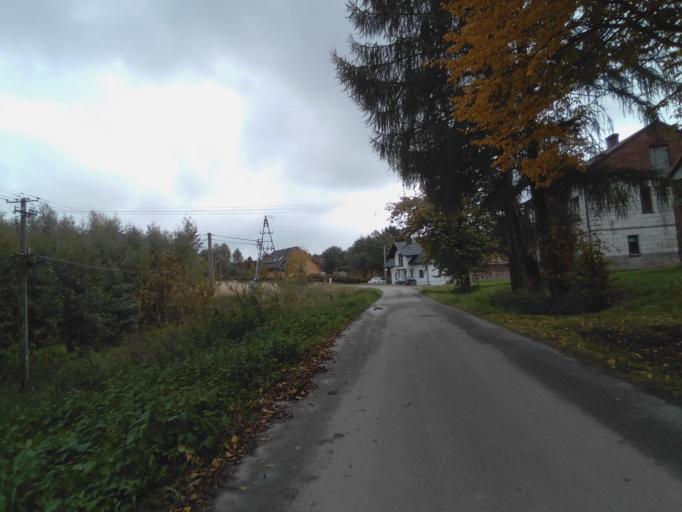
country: PL
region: Subcarpathian Voivodeship
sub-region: Powiat strzyzowski
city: Gwoznica Gorna
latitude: 49.8352
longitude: 22.0111
